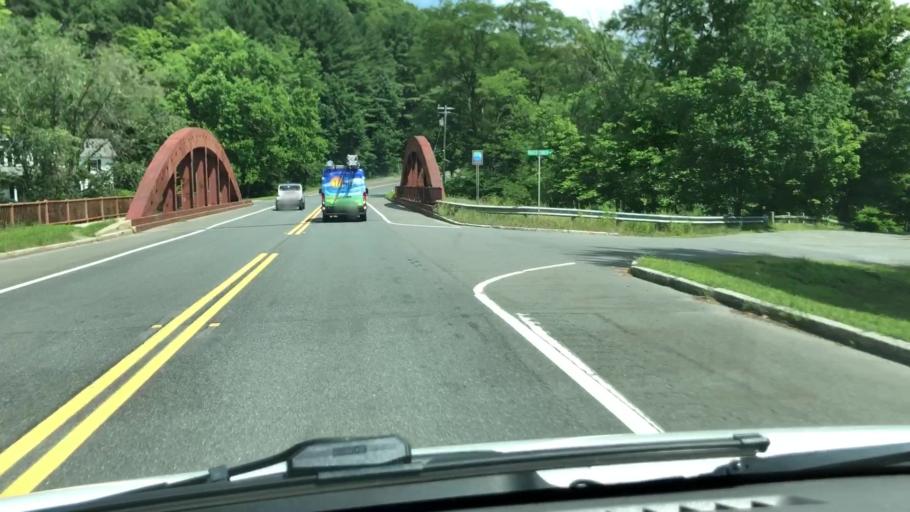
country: US
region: Massachusetts
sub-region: Hampshire County
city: Chesterfield
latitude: 42.4559
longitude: -72.8853
